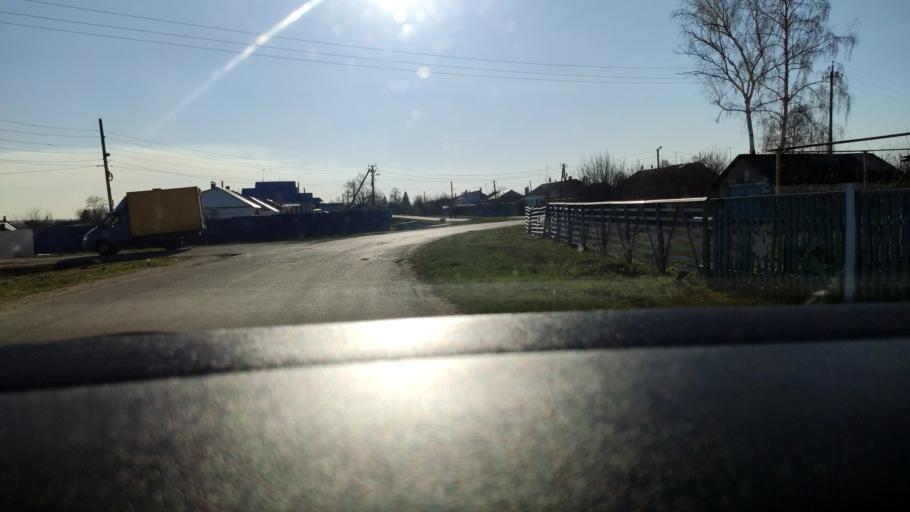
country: RU
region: Voronezj
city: Maslovka
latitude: 51.5013
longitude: 39.2961
